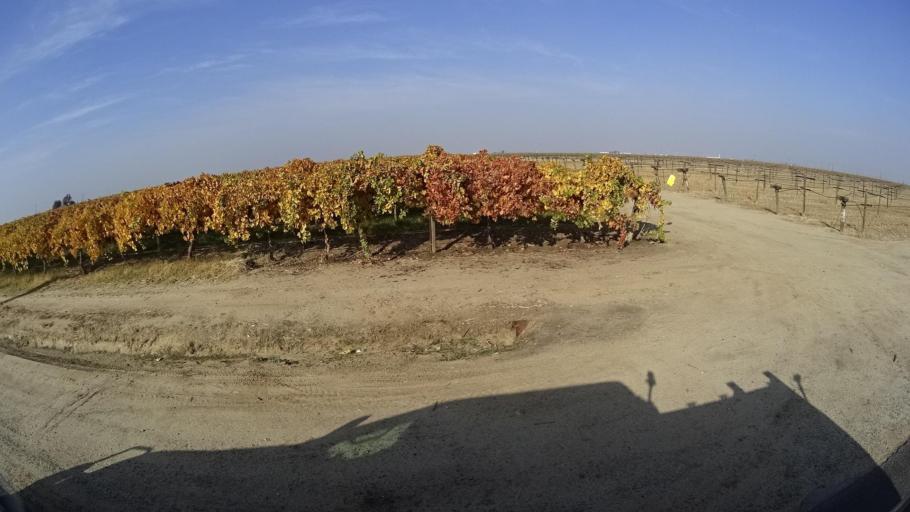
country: US
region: California
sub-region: Tulare County
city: Richgrove
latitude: 35.7762
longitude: -119.1296
